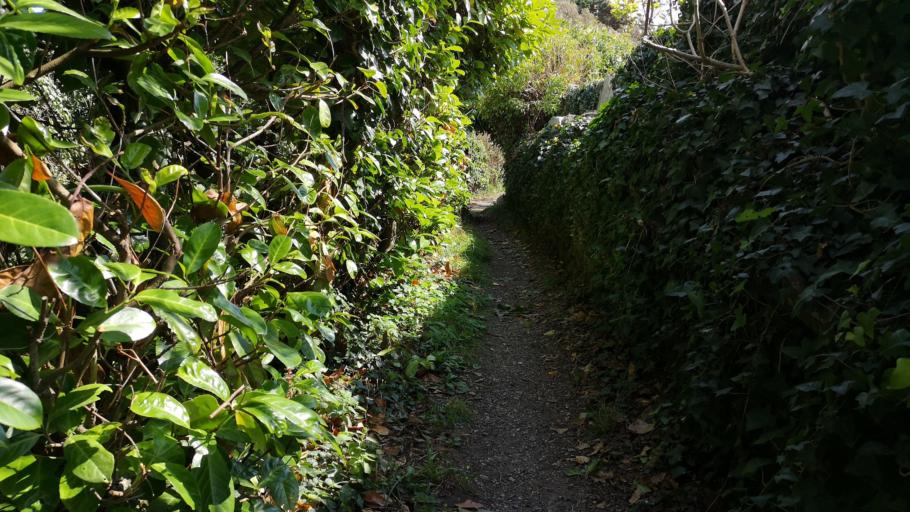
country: GB
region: England
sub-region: Isle of Wight
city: Ventnor
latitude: 50.5883
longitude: -1.2316
